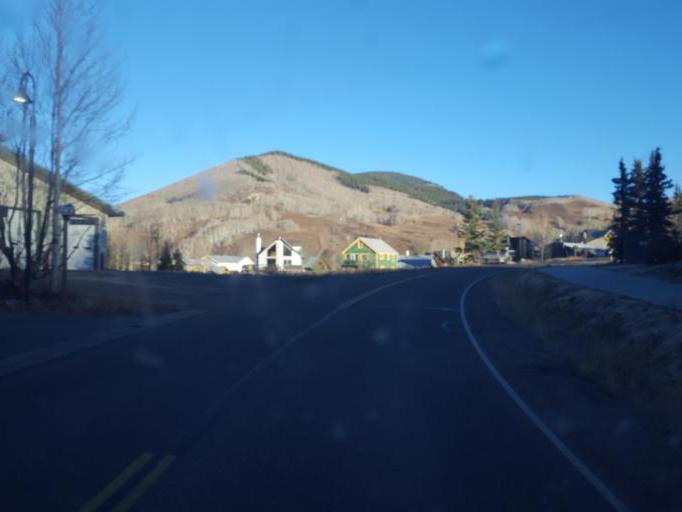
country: US
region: Colorado
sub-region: Gunnison County
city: Crested Butte
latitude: 38.9047
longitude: -106.9708
